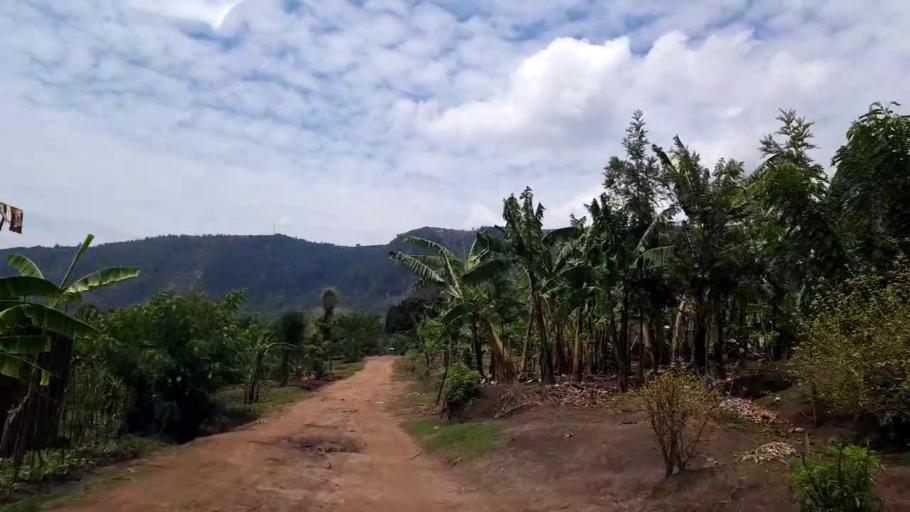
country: RW
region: Northern Province
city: Byumba
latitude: -1.4908
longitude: 30.1985
